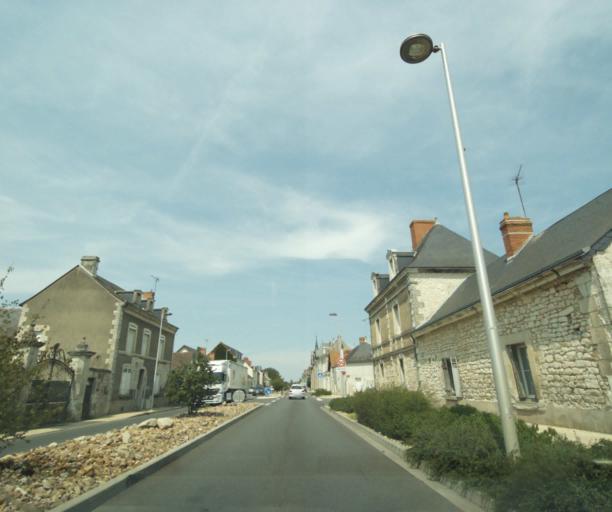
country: FR
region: Poitou-Charentes
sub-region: Departement de la Vienne
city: Antran
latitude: 46.8728
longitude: 0.5630
